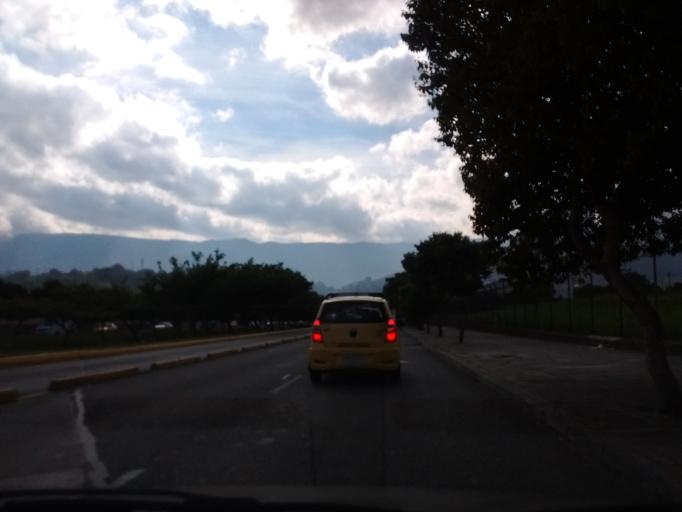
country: CO
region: Antioquia
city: Medellin
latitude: 6.2315
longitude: -75.5888
